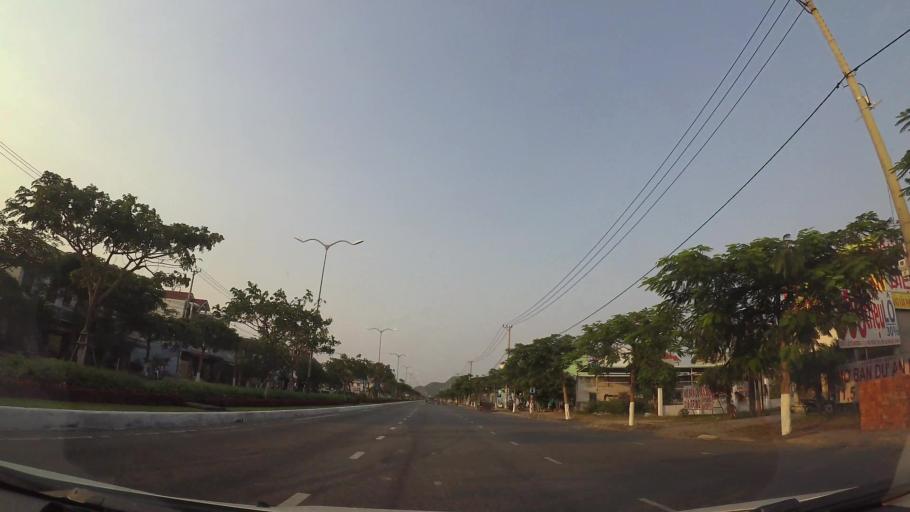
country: VN
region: Da Nang
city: Ngu Hanh Son
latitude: 15.9900
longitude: 108.2577
